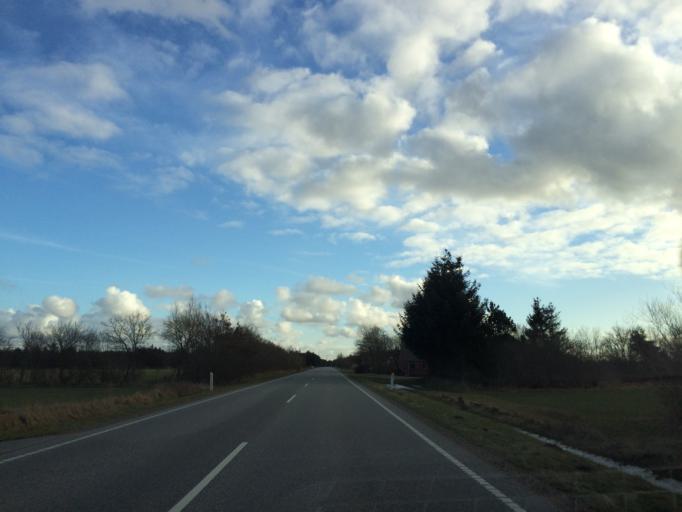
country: DK
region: Central Jutland
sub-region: Holstebro Kommune
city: Ulfborg
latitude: 56.3747
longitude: 8.3305
